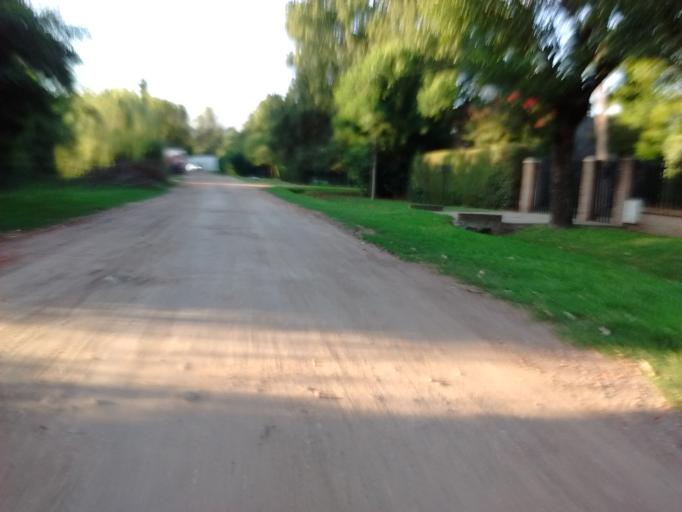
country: AR
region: Santa Fe
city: Funes
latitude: -32.9210
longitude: -60.8287
